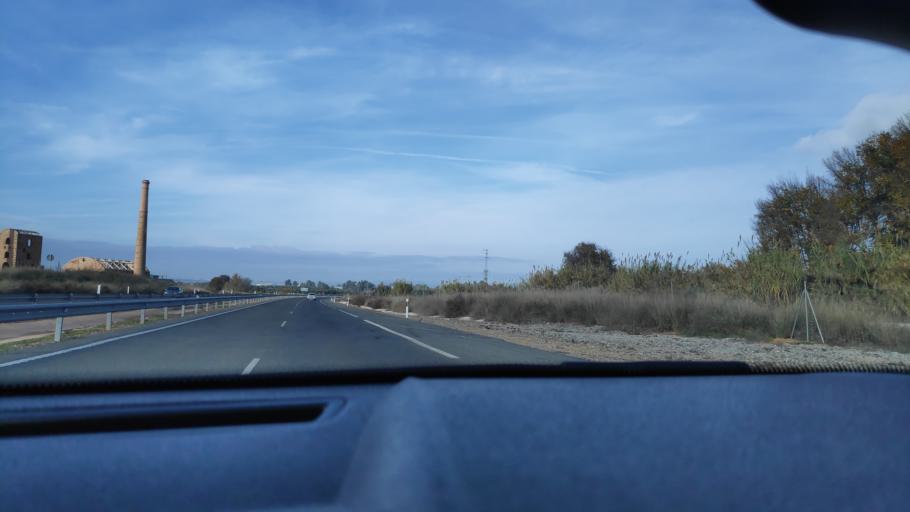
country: ES
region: Andalusia
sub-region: Provincia de Jaen
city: Linares
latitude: 38.0903
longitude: -3.6719
